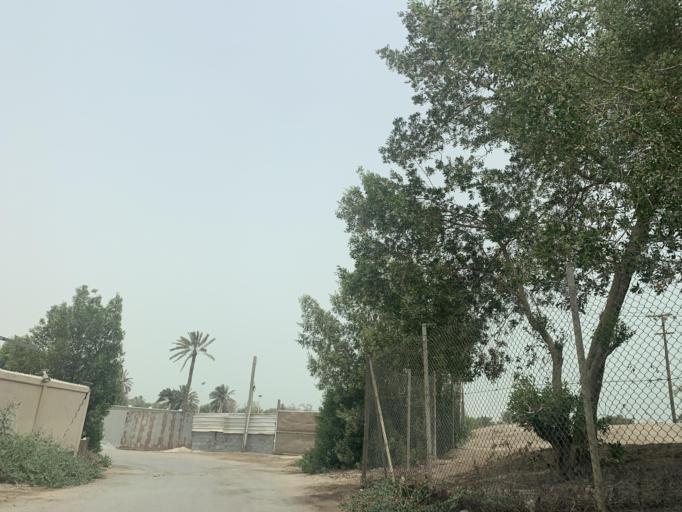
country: BH
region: Manama
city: Jidd Hafs
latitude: 26.2315
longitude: 50.5190
